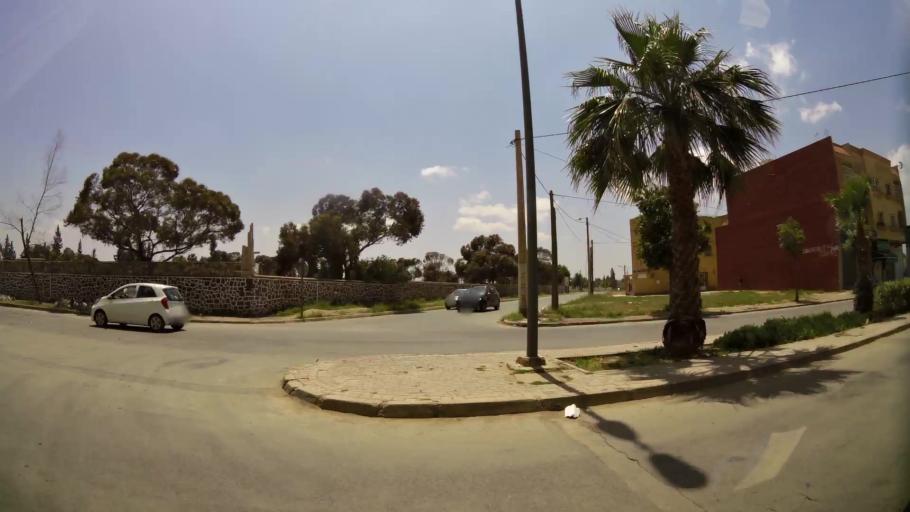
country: MA
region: Oriental
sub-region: Oujda-Angad
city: Oujda
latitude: 34.6925
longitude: -1.8985
